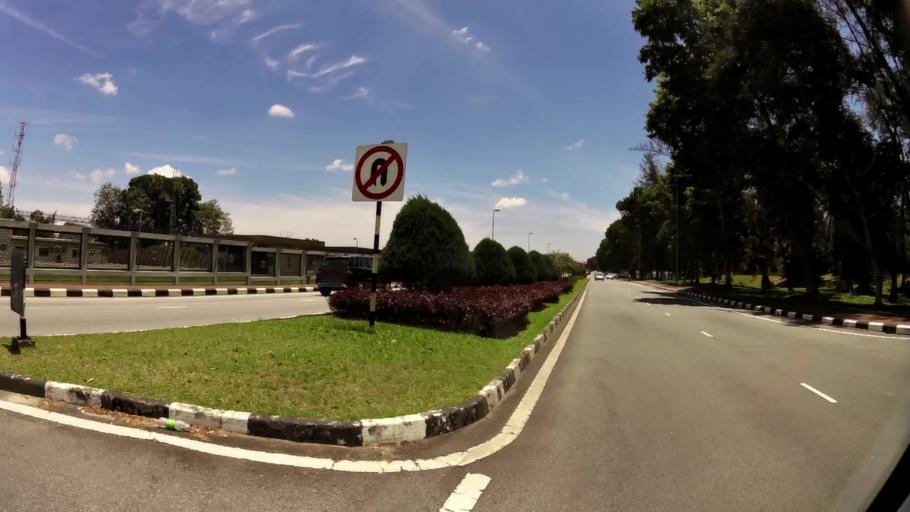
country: BN
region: Brunei and Muara
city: Bandar Seri Begawan
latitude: 4.9272
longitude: 114.9385
